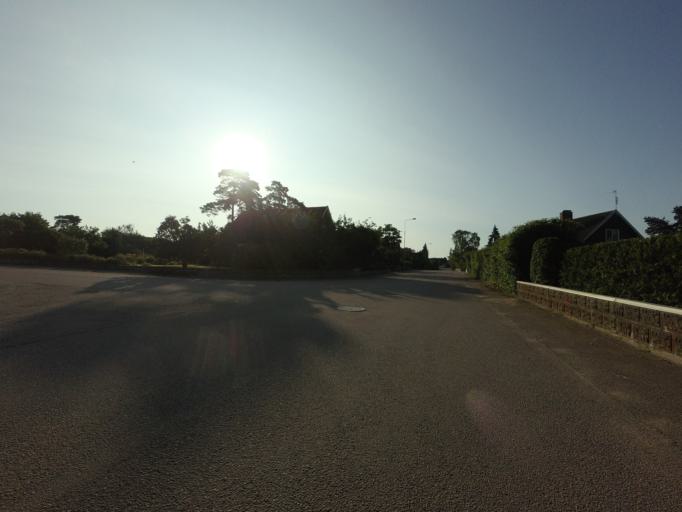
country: SE
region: Skane
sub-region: Landskrona
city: Asmundtorp
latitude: 55.8531
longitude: 12.9177
